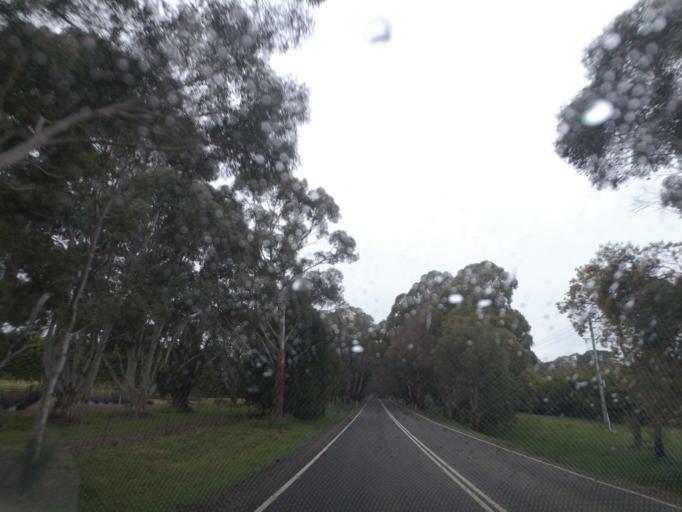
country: AU
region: Victoria
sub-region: Hume
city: Sunbury
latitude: -37.3502
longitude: 144.6354
